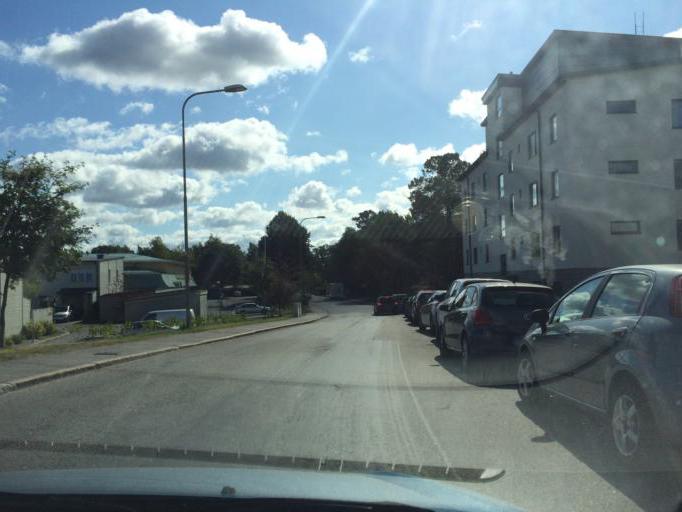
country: SE
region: Stockholm
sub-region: Nacka Kommun
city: Nacka
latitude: 59.2780
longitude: 18.1399
